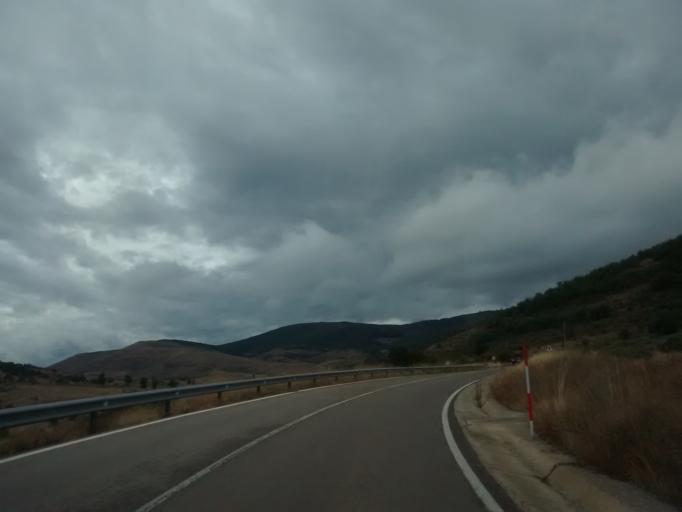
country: ES
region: Cantabria
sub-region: Provincia de Cantabria
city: Mataporquera
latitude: 42.8891
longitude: -4.0756
